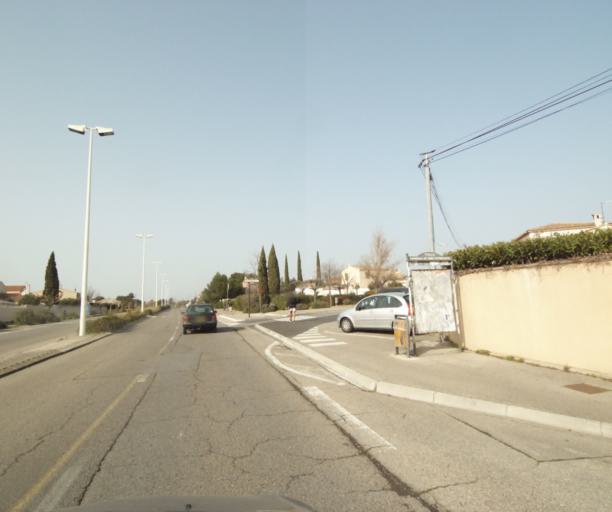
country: FR
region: Provence-Alpes-Cote d'Azur
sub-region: Departement des Bouches-du-Rhone
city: Vitrolles
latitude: 43.4509
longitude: 5.2453
